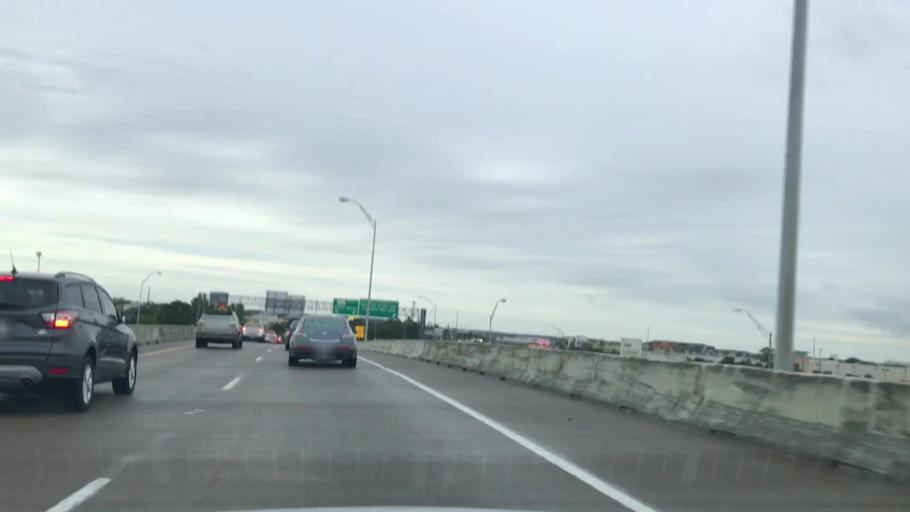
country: US
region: Texas
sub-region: Dallas County
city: Coppell
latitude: 32.9650
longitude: -97.0368
